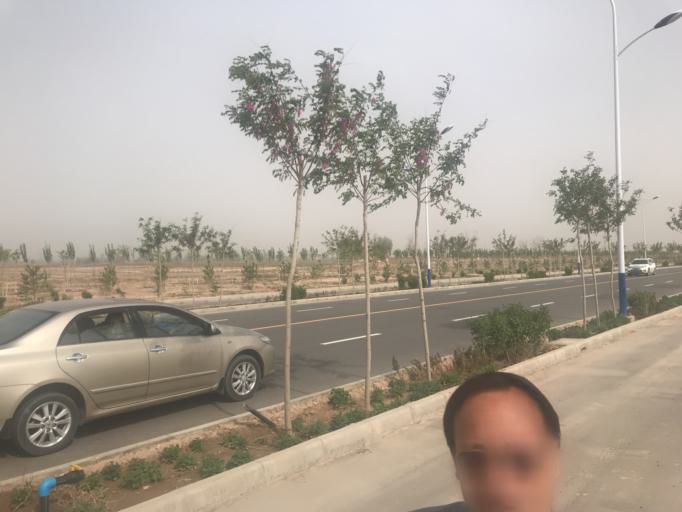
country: CN
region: Gansu Sheng
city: Wuwei
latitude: 38.0199
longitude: 102.5380
